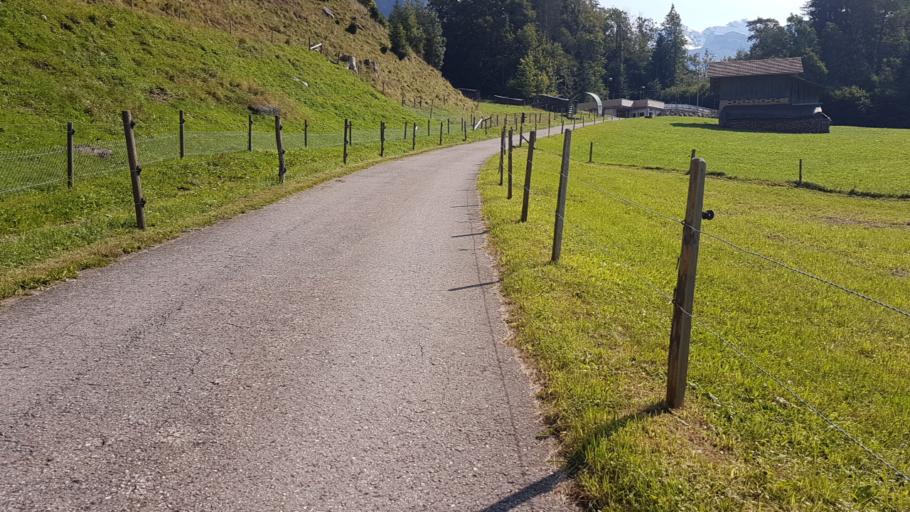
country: CH
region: Bern
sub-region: Frutigen-Niedersimmental District
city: Frutigen
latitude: 46.5884
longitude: 7.7220
